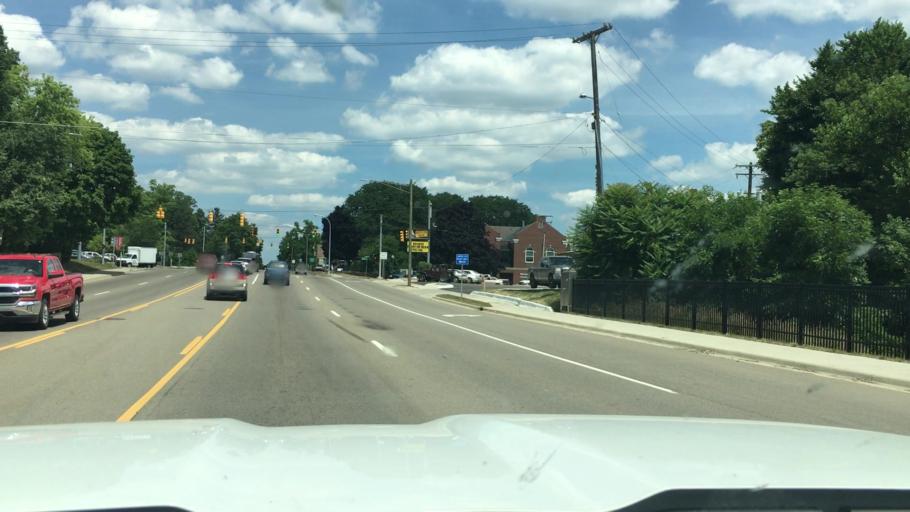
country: US
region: Michigan
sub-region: Lapeer County
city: Lapeer
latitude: 43.0498
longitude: -83.3186
